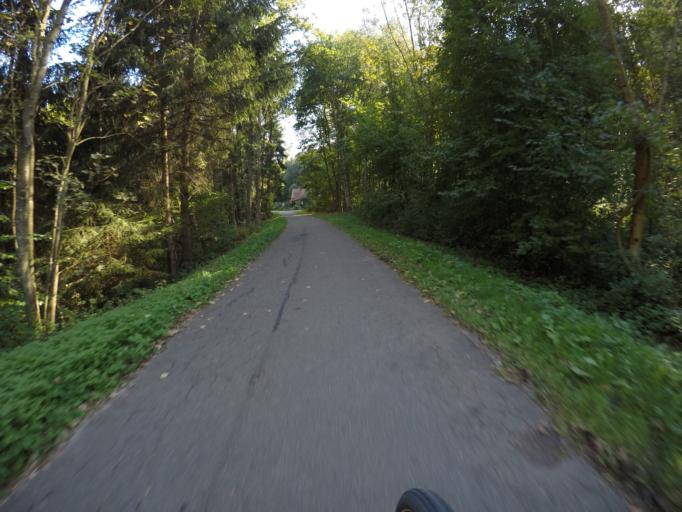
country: DE
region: Baden-Wuerttemberg
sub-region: Regierungsbezirk Stuttgart
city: Steinenbronn
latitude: 48.6758
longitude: 9.1260
